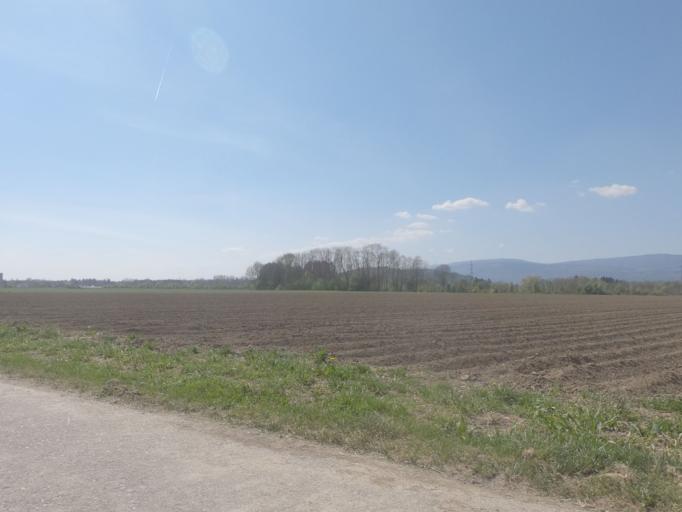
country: CH
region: Bern
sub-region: Seeland District
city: Worben
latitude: 47.1088
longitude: 7.3332
